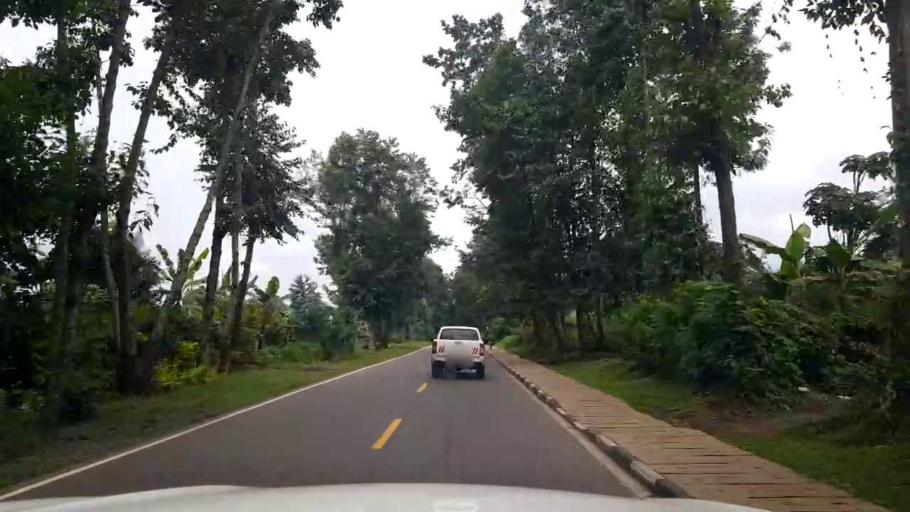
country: RW
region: Northern Province
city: Musanze
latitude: -1.4569
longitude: 29.6105
